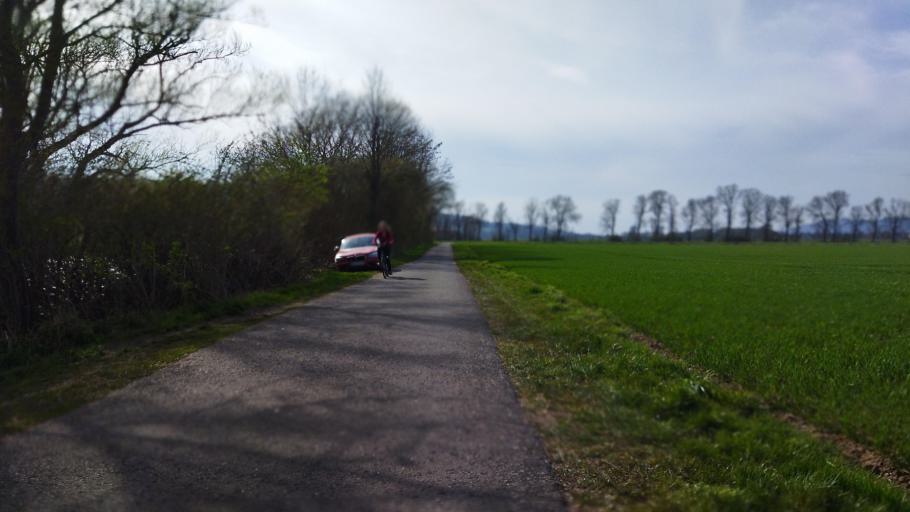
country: DE
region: Lower Saxony
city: Hessisch Oldendorf
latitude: 52.1635
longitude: 9.2193
